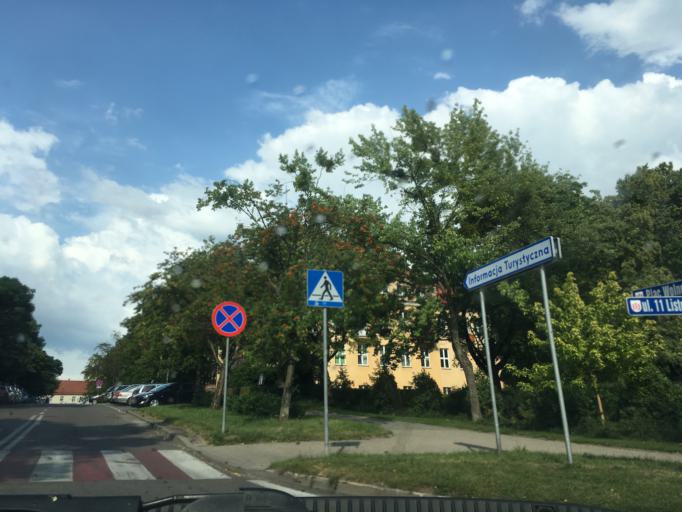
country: PL
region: Warmian-Masurian Voivodeship
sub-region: Powiat olecki
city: Olecko
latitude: 54.0381
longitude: 22.5028
